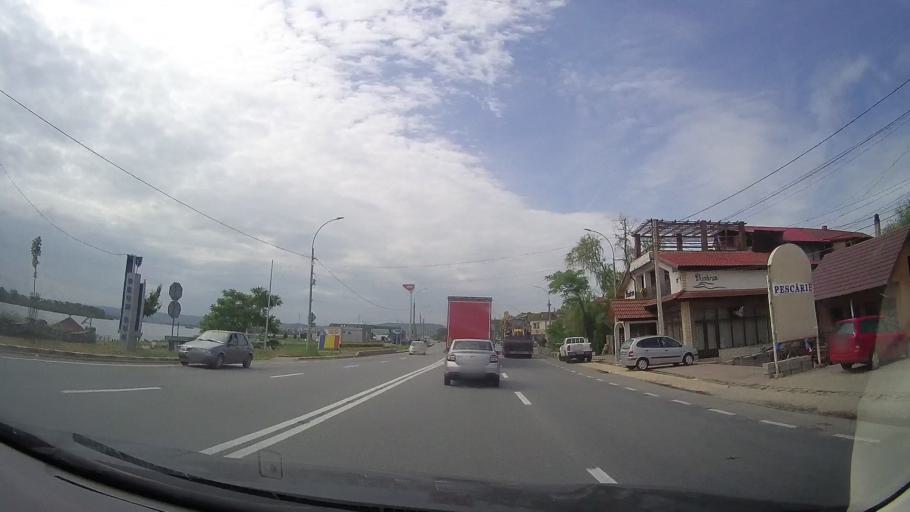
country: RO
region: Mehedinti
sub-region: Comuna Simian
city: Simian
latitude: 44.6139
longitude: 22.7002
